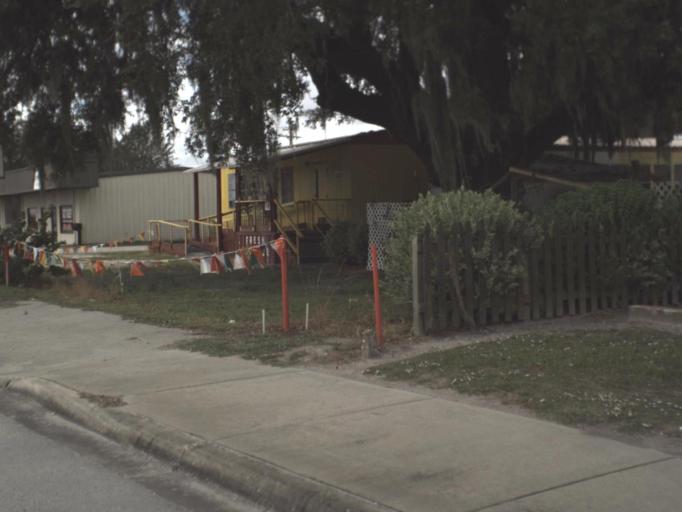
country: US
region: Florida
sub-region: Hardee County
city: Wauchula
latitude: 27.5374
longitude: -81.8095
